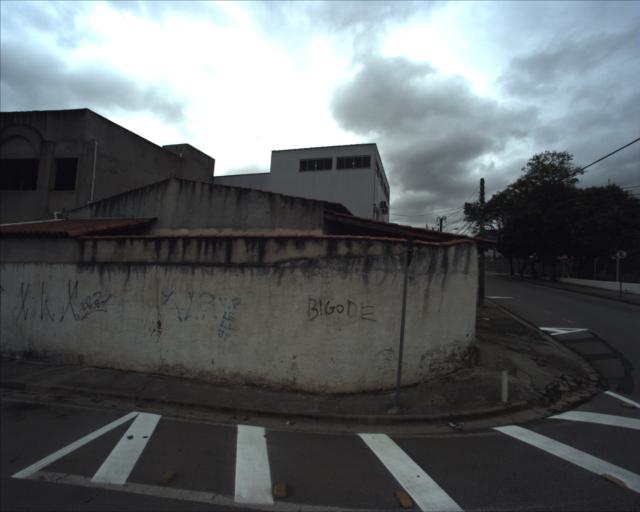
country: BR
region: Sao Paulo
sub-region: Sorocaba
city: Sorocaba
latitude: -23.4726
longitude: -47.4571
